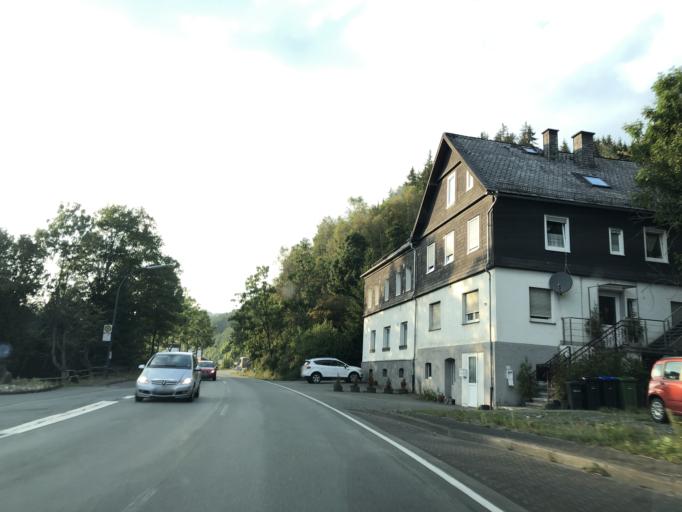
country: DE
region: North Rhine-Westphalia
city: Hallenberg
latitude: 51.1509
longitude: 8.5814
